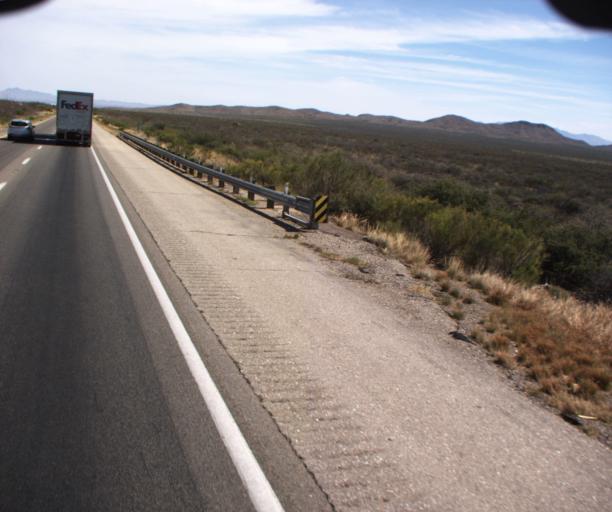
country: US
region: Arizona
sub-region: Cochise County
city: Willcox
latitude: 32.1193
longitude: -110.0172
